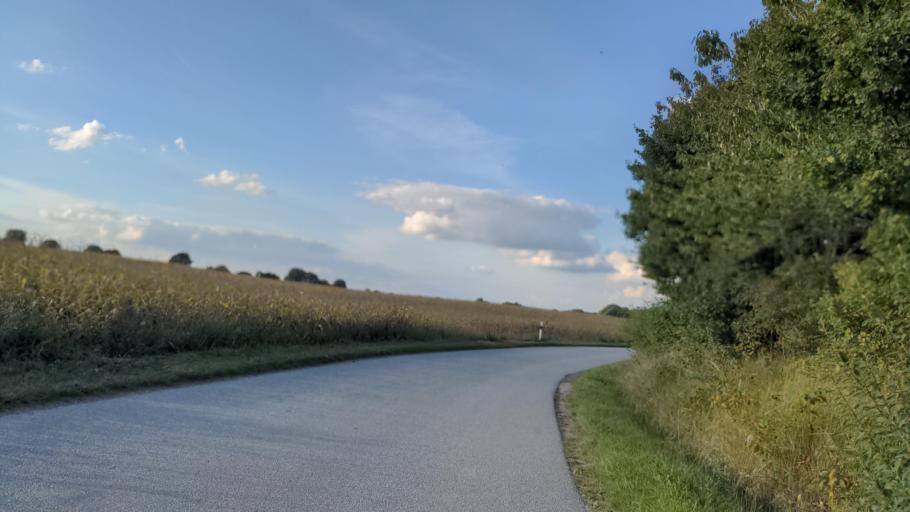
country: DE
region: Schleswig-Holstein
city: Ahrensbok
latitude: 53.9821
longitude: 10.6255
